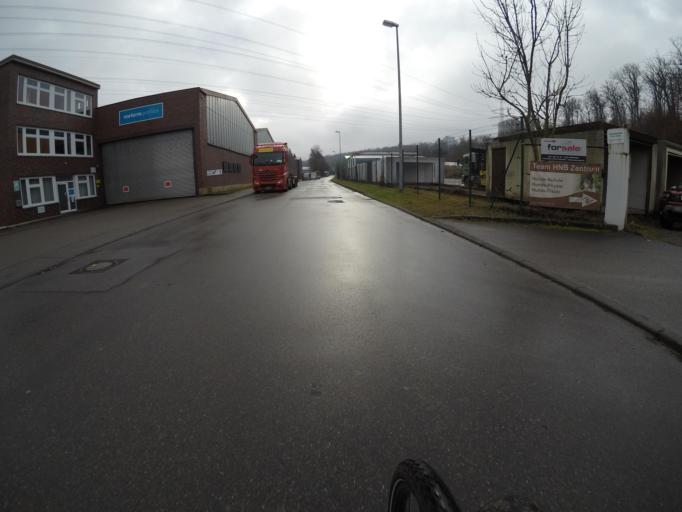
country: DE
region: Baden-Wuerttemberg
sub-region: Regierungsbezirk Stuttgart
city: Nurtingen
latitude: 48.6077
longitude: 9.3467
